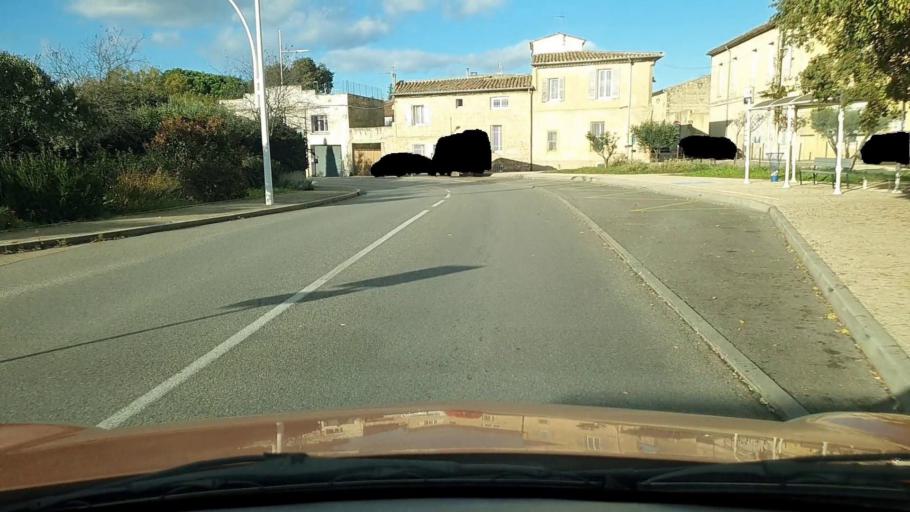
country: FR
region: Languedoc-Roussillon
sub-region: Departement du Gard
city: Vauvert
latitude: 43.6901
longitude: 4.2738
